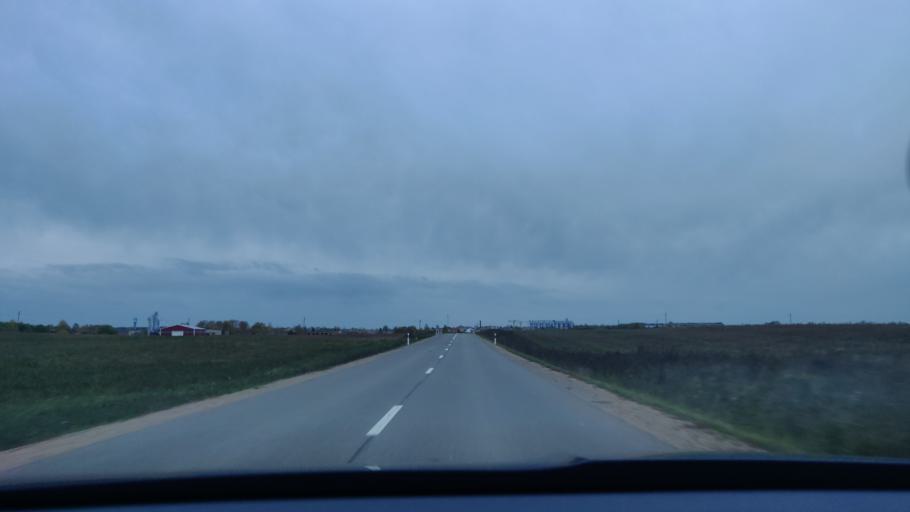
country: LT
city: Lentvaris
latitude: 54.6055
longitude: 24.9995
